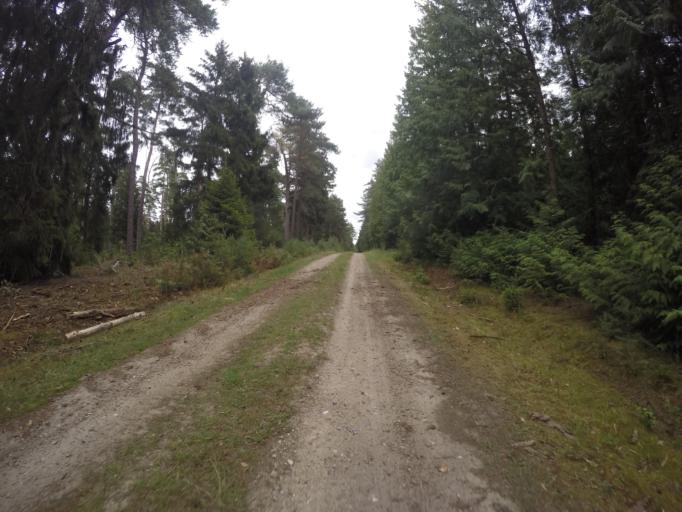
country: DE
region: Lower Saxony
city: Thomasburg
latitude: 53.2440
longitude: 10.6905
